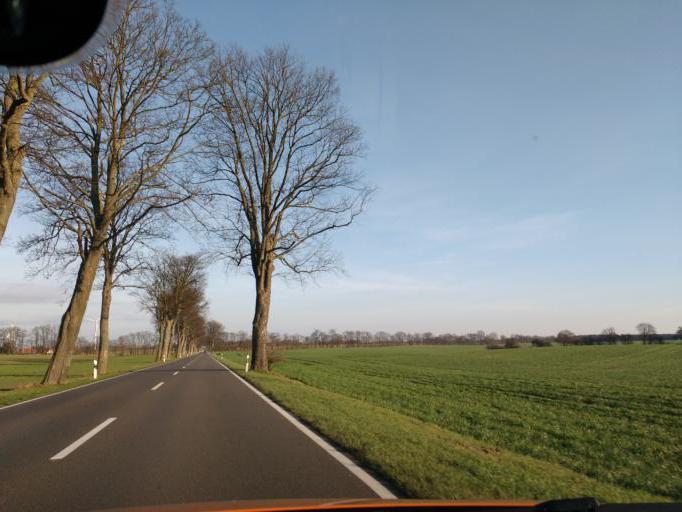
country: DE
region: Brandenburg
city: Protzel
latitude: 52.6642
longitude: 14.0510
